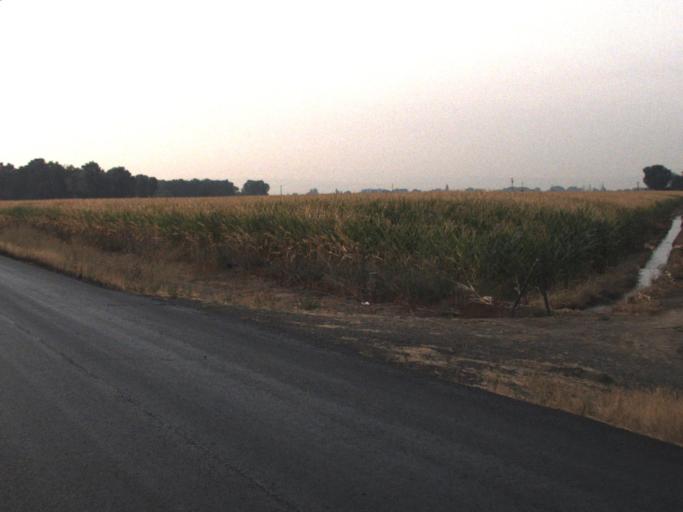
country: US
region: Washington
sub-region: Yakima County
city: Wapato
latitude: 46.4246
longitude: -120.4067
